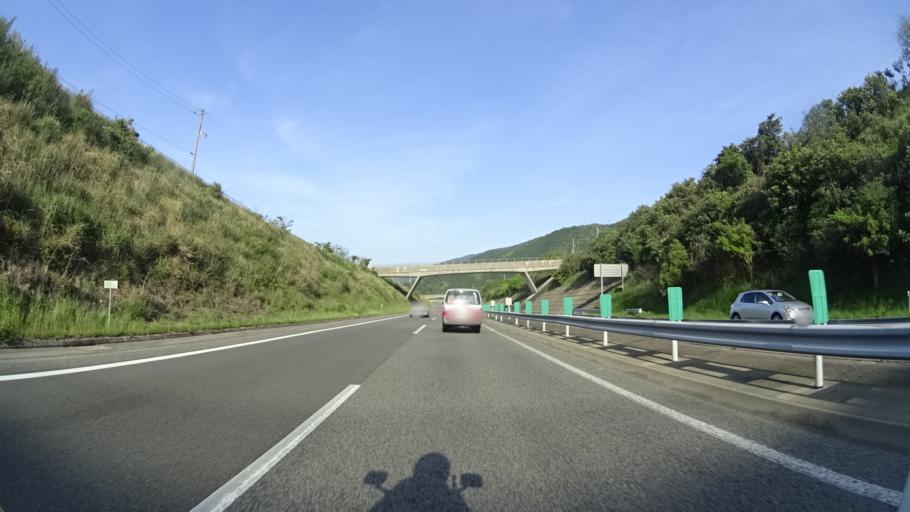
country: JP
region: Ehime
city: Kawanoecho
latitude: 33.9597
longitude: 133.4881
